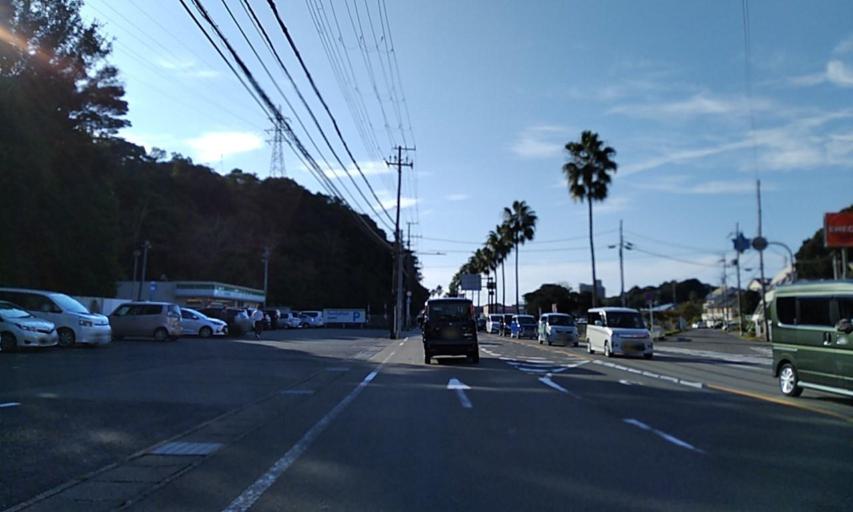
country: JP
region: Wakayama
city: Tanabe
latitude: 33.6795
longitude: 135.3689
